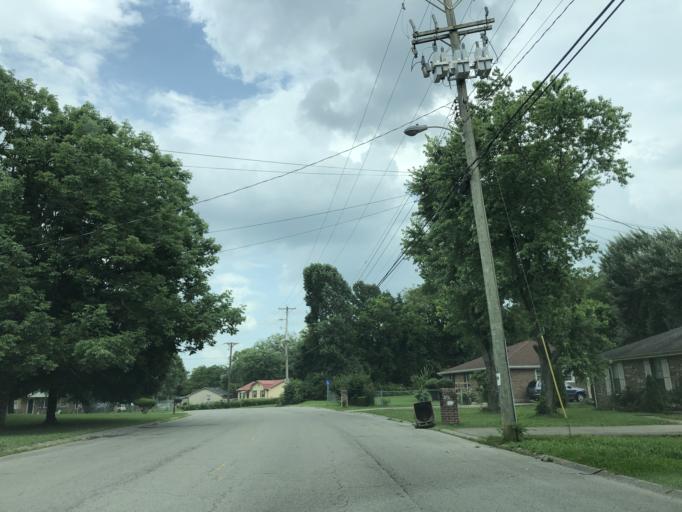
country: US
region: Tennessee
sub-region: Williamson County
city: Brentwood Estates
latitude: 36.0563
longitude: -86.6873
